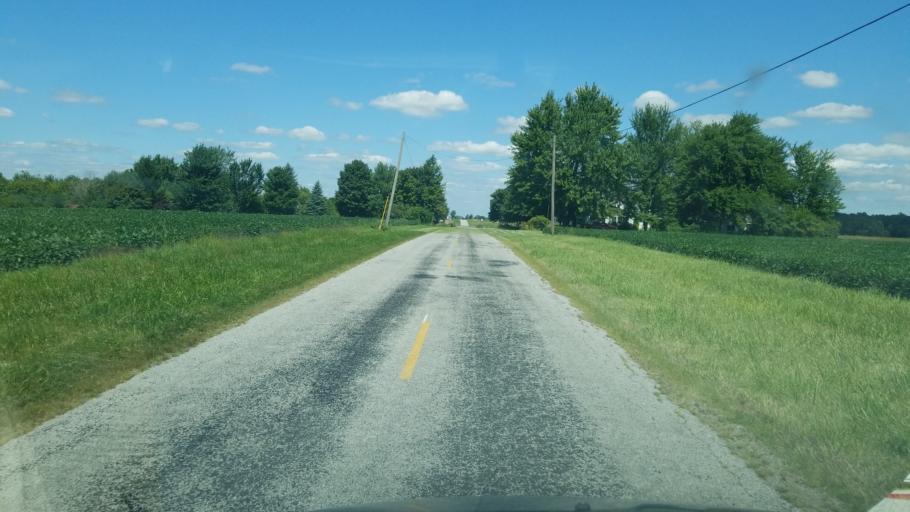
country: US
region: Ohio
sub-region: Fulton County
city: Delta
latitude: 41.7119
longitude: -84.0178
